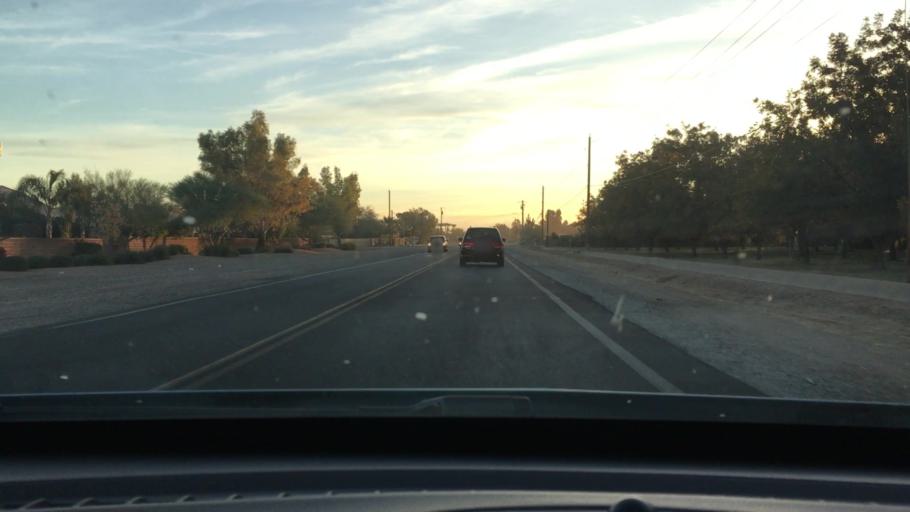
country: US
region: Arizona
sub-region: Maricopa County
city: Sun Lakes
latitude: 33.2336
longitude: -111.8039
